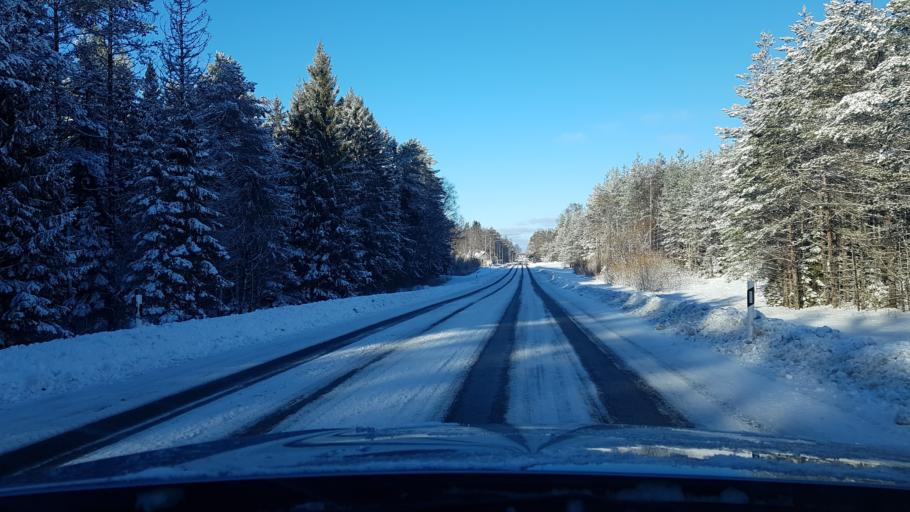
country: EE
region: Hiiumaa
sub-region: Kaerdla linn
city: Kardla
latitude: 58.9758
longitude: 22.7618
